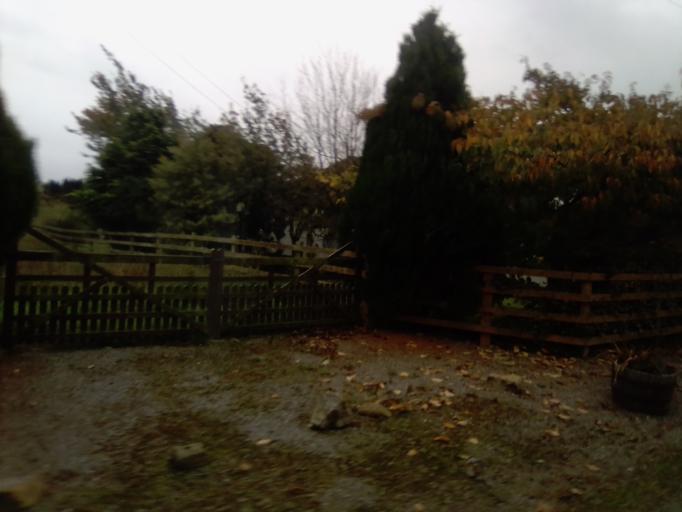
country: IE
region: Munster
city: Nenagh Bridge
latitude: 52.8982
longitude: -8.0737
